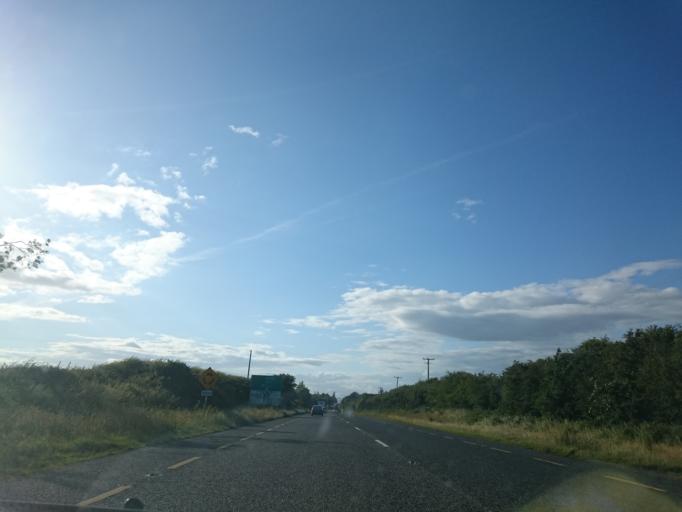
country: IE
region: Leinster
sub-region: Loch Garman
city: Loch Garman
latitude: 52.3198
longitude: -6.4978
